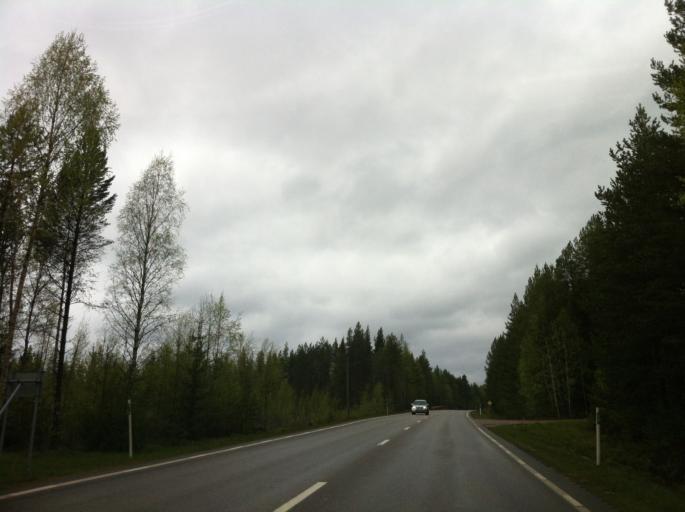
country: SE
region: Jaemtland
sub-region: Harjedalens Kommun
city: Sveg
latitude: 62.0478
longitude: 14.3267
